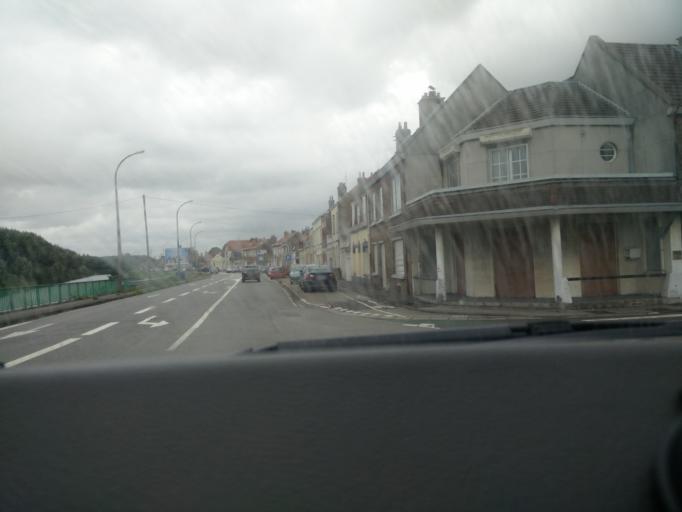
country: FR
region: Nord-Pas-de-Calais
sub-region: Departement du Nord
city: Coudekerque-Branche
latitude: 51.0019
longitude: 2.3837
